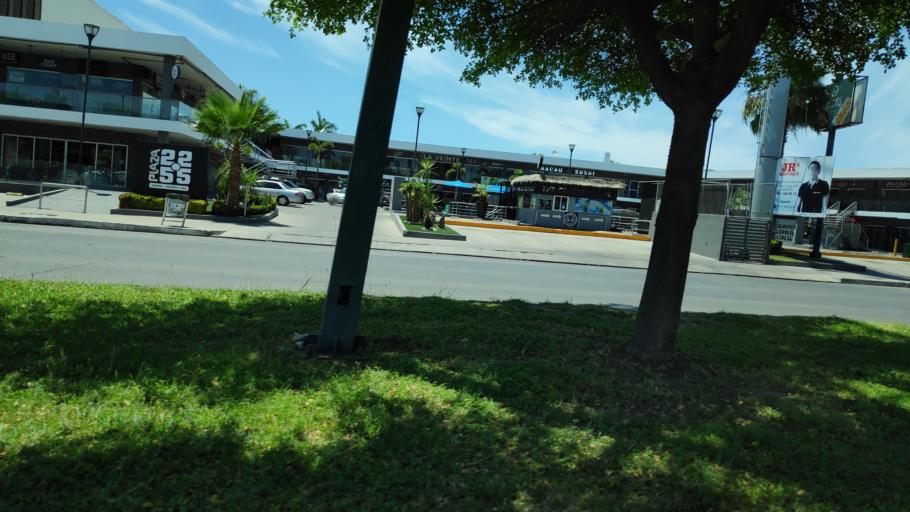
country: MX
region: Sinaloa
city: Culiacan
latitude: 24.8303
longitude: -107.3992
